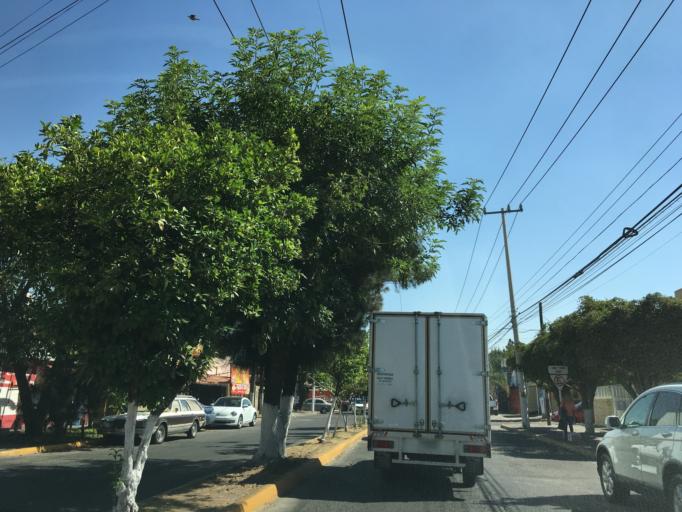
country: MX
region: Jalisco
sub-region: Tlajomulco de Zuniga
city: La Tijera
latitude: 20.6213
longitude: -103.4166
